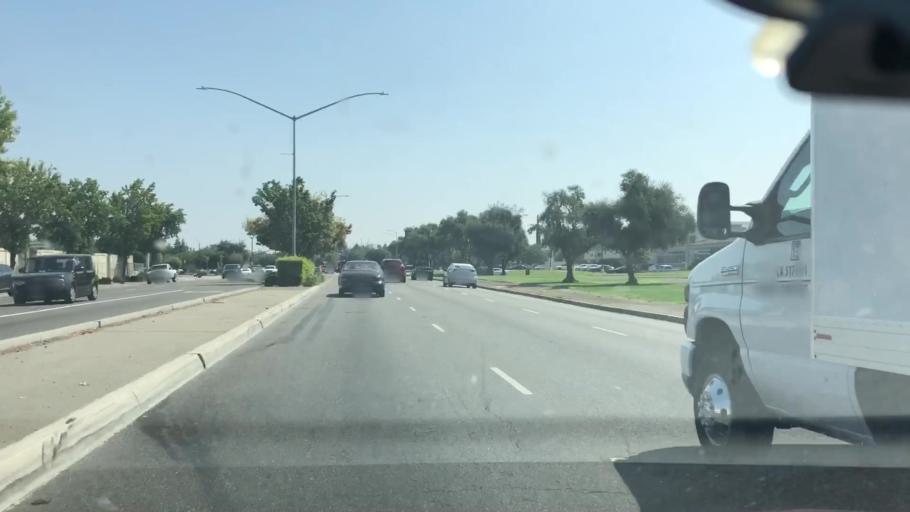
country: US
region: California
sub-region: San Joaquin County
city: Lincoln Village
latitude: 37.9906
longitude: -121.3154
